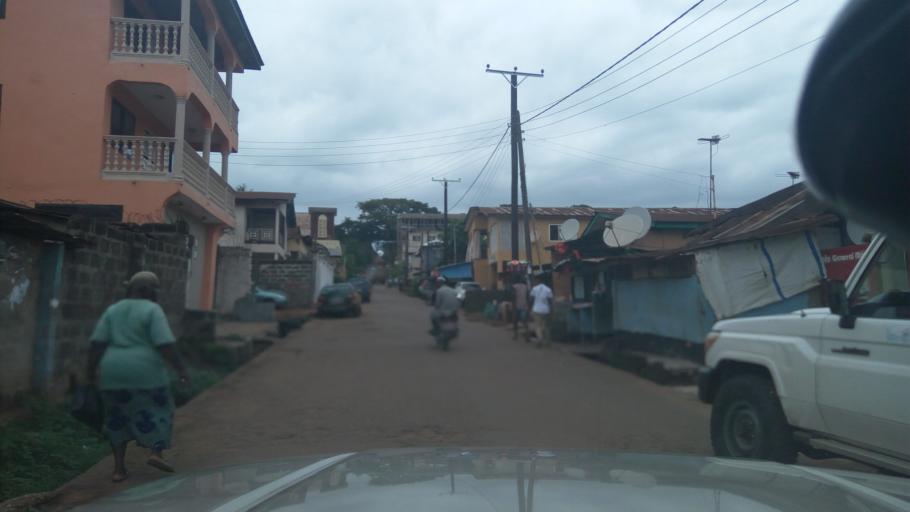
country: SL
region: Western Area
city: Freetown
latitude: 8.4949
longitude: -13.2639
